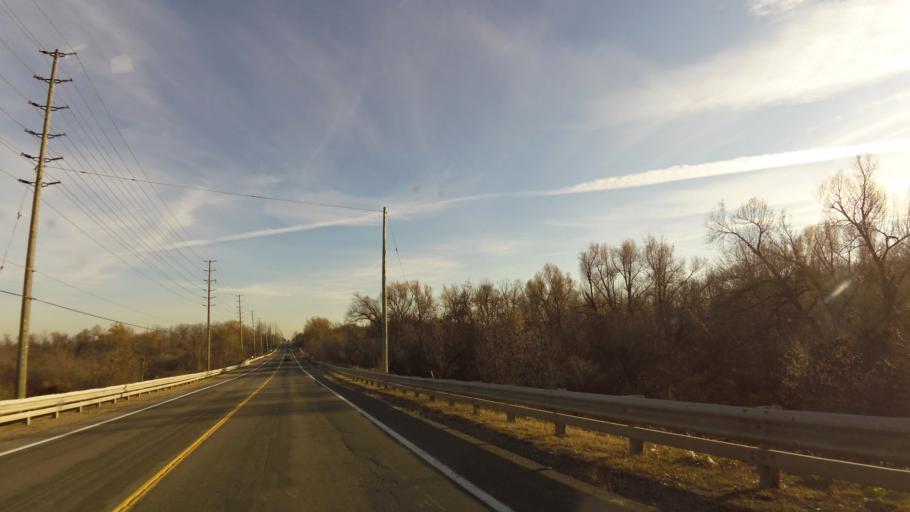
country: CA
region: Ontario
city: Brampton
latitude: 43.7691
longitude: -79.7060
